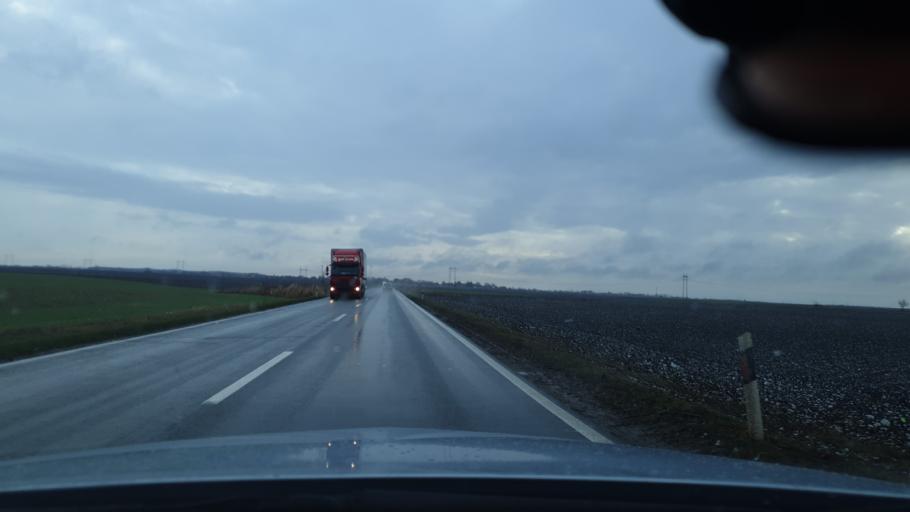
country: RS
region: Autonomna Pokrajina Vojvodina
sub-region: Juznobanatski Okrug
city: Kovin
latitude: 44.8291
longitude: 20.8376
